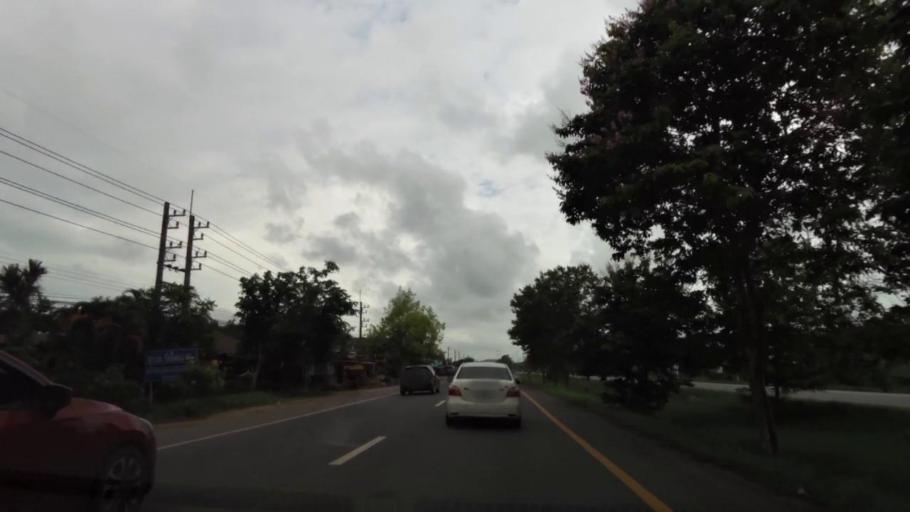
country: TH
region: Chanthaburi
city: Na Yai Am
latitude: 12.7253
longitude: 101.9337
